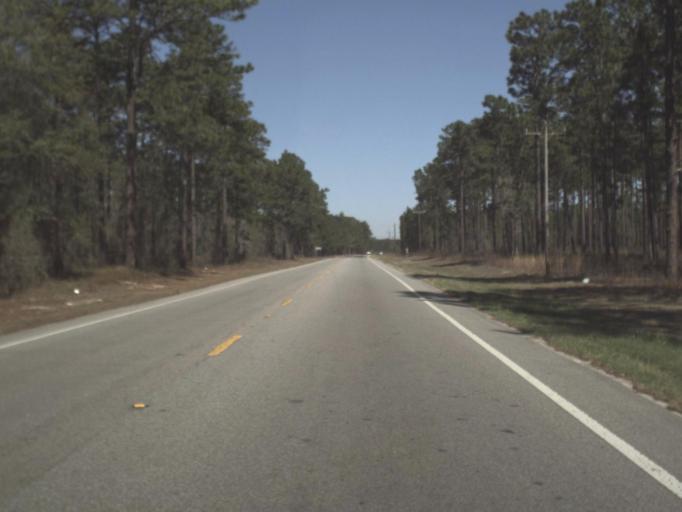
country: US
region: Florida
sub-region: Leon County
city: Woodville
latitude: 30.3358
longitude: -84.3112
